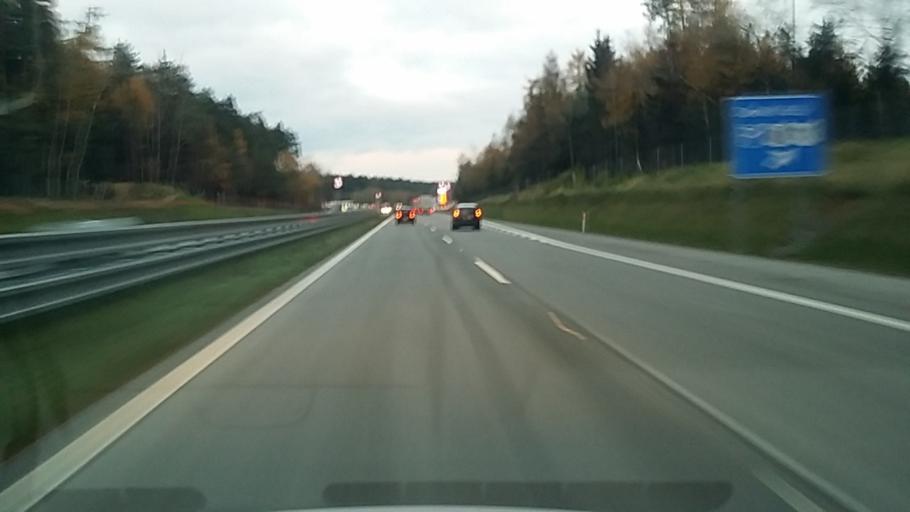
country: CZ
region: Vysocina
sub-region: Okres Zd'ar nad Sazavou
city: Velka Bites
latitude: 49.2705
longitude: 16.2719
